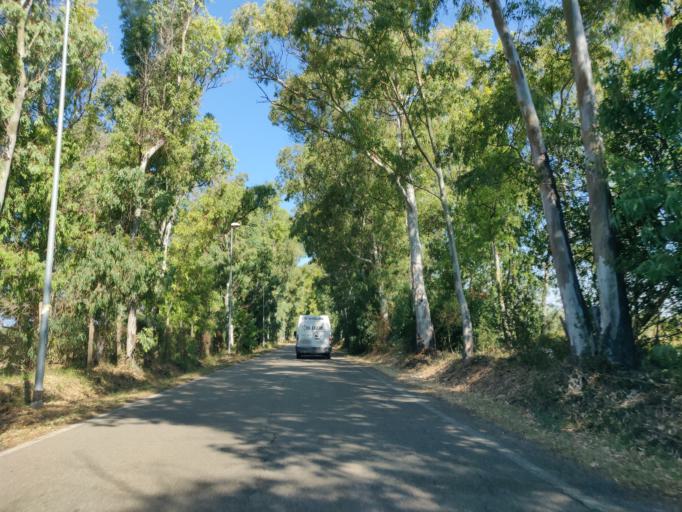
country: IT
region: Latium
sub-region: Citta metropolitana di Roma Capitale
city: Aurelia
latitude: 42.1568
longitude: 11.7529
